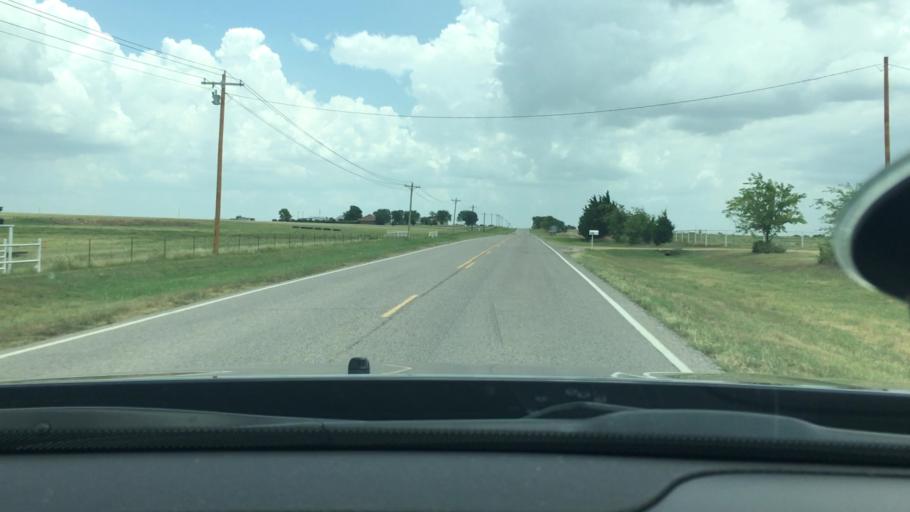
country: US
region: Oklahoma
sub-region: Love County
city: Marietta
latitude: 33.9403
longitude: -97.0674
